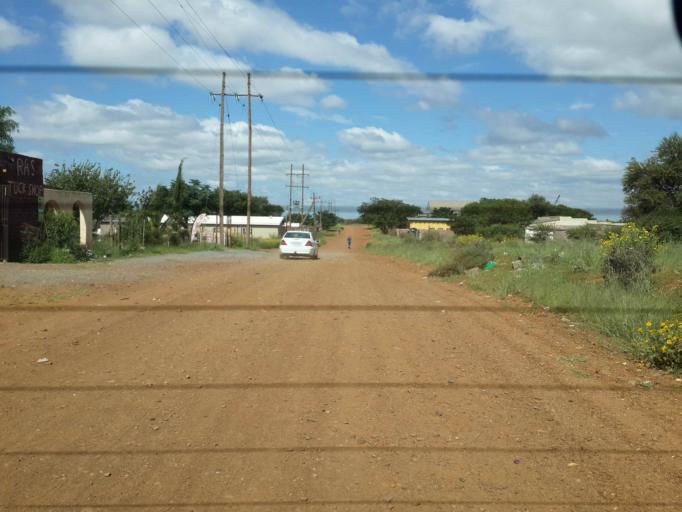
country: ZA
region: Northern Cape
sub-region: Siyanda District Municipality
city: Danielskuil
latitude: -28.1911
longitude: 23.5428
